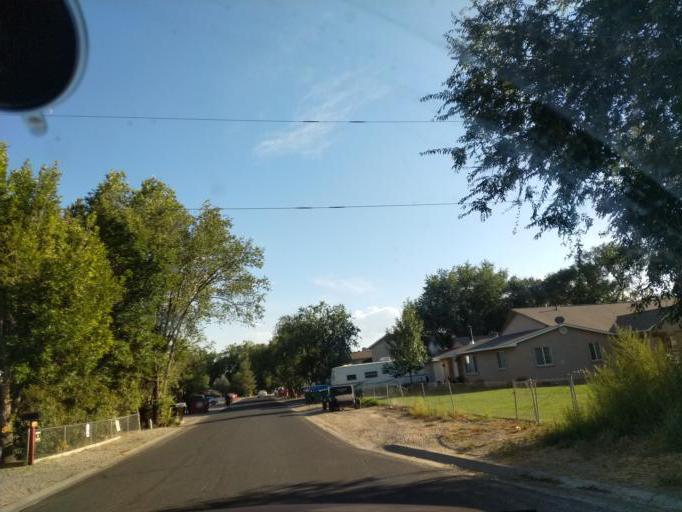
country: US
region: Colorado
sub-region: Mesa County
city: Clifton
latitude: 39.0729
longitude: -108.4569
